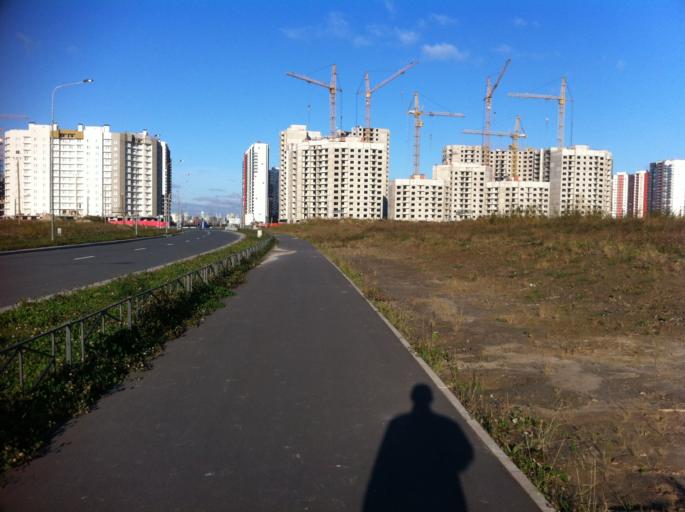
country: RU
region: St.-Petersburg
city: Sosnovaya Polyana
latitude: 59.8646
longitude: 30.1549
